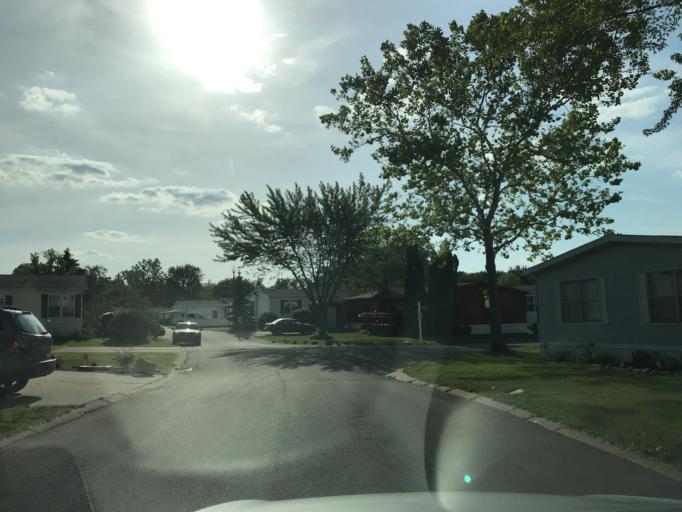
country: US
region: Michigan
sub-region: Oakland County
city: Walled Lake
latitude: 42.5142
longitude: -83.4613
